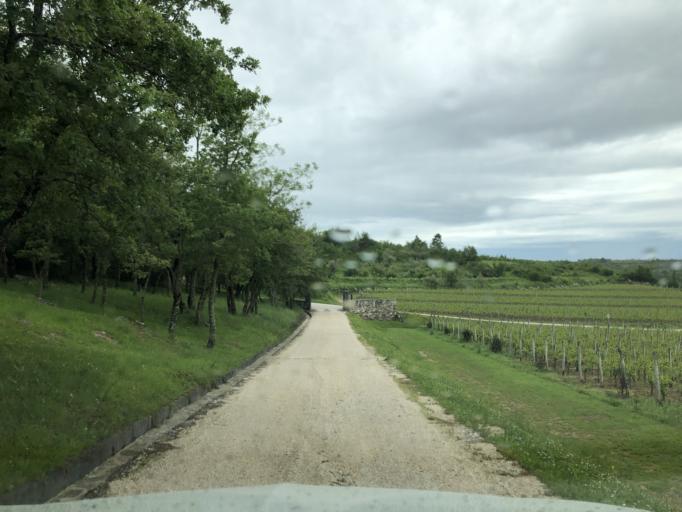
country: HR
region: Istarska
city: Buje
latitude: 45.4306
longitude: 13.6990
